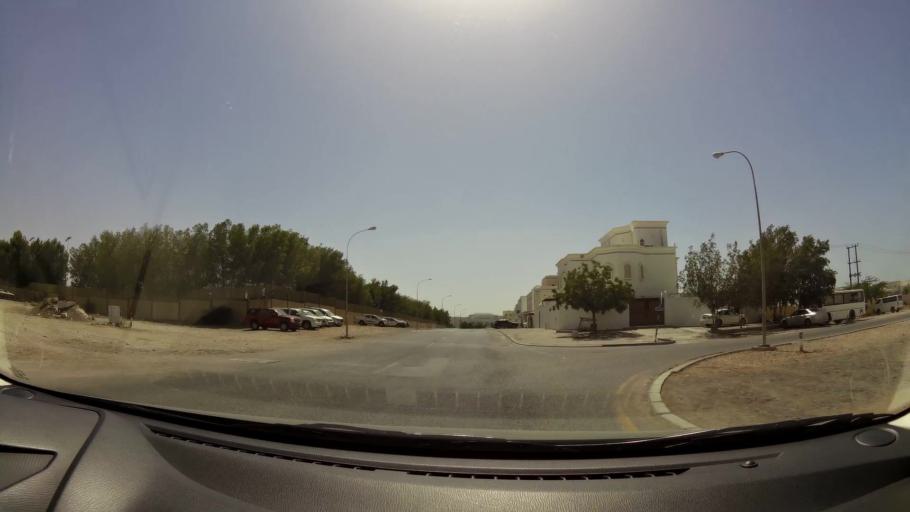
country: OM
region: Muhafazat Masqat
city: Bawshar
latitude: 23.5969
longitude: 58.3578
